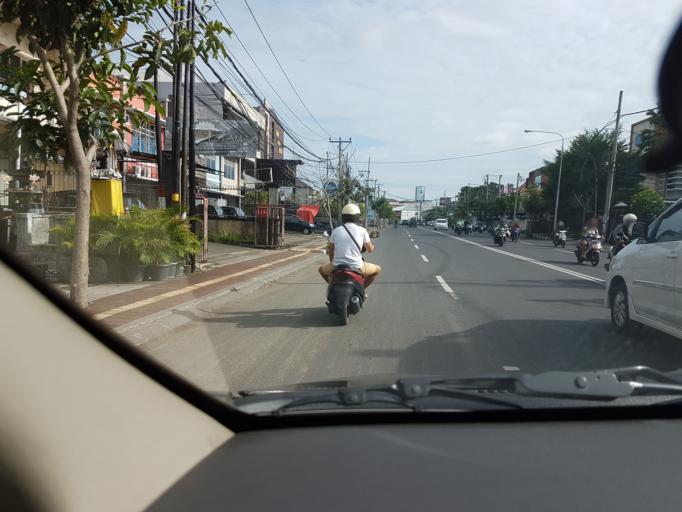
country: ID
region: Bali
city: Karyadharma
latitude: -8.6797
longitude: 115.1899
